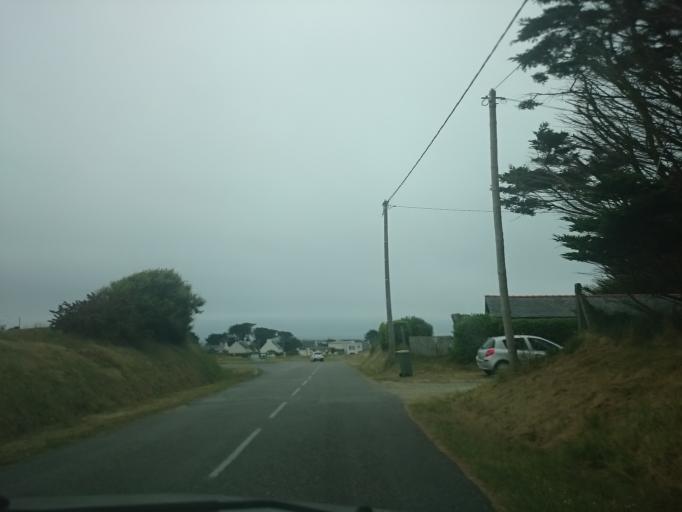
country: FR
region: Brittany
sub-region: Departement du Finistere
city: Saint-Pabu
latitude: 48.5717
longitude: -4.6260
